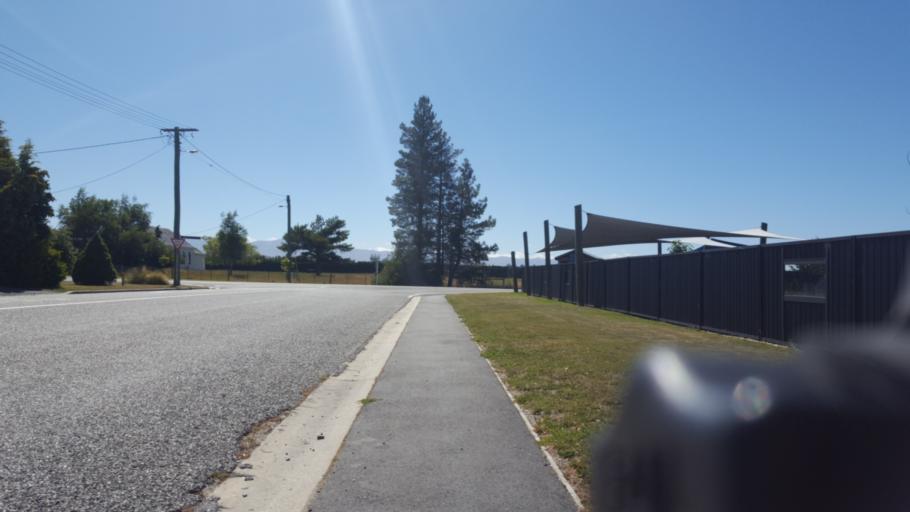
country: NZ
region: Otago
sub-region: Dunedin City
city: Dunedin
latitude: -45.1237
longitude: 170.1000
